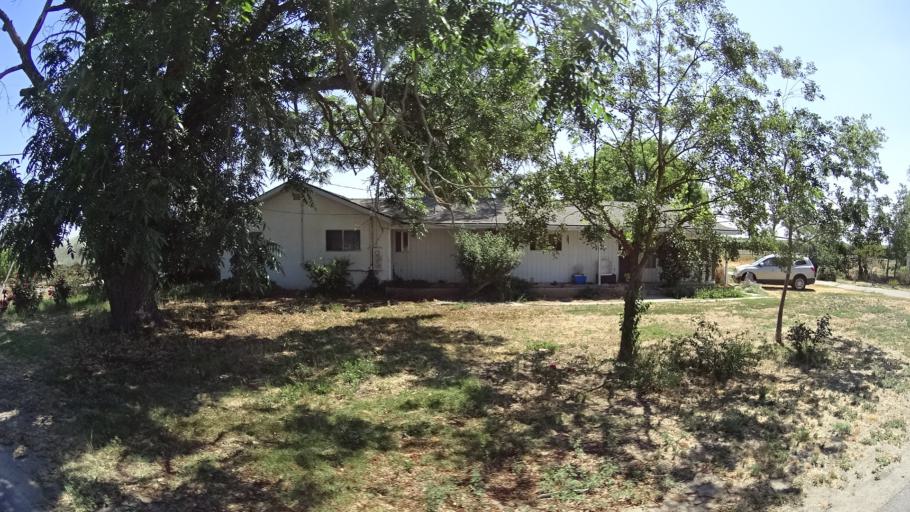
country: US
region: California
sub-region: Fresno County
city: Kingsburg
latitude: 36.4486
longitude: -119.6005
